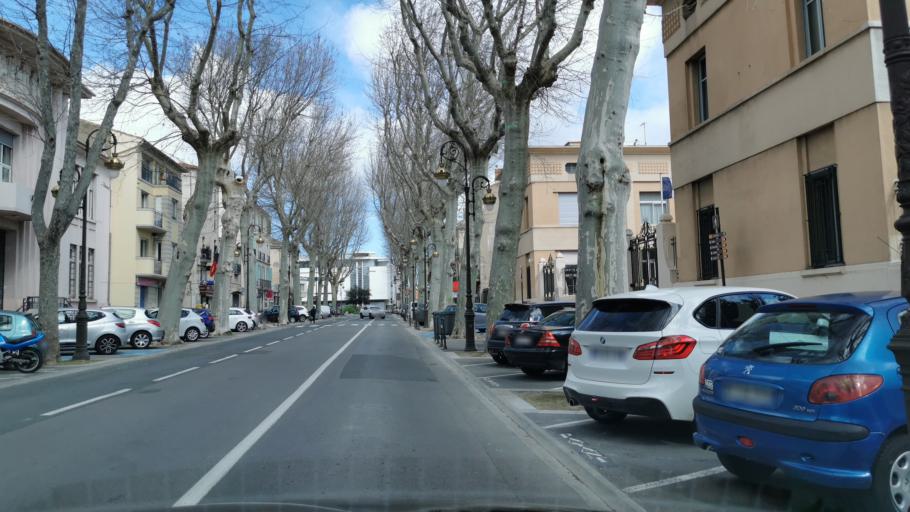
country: FR
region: Languedoc-Roussillon
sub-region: Departement de l'Aude
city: Narbonne
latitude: 43.1840
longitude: 3.0088
